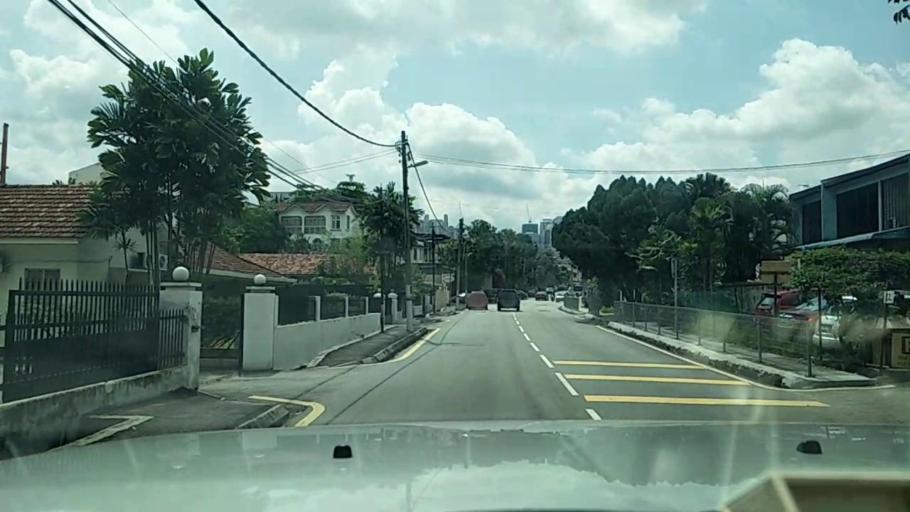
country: MY
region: Kuala Lumpur
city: Kuala Lumpur
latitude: 3.1284
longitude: 101.6754
